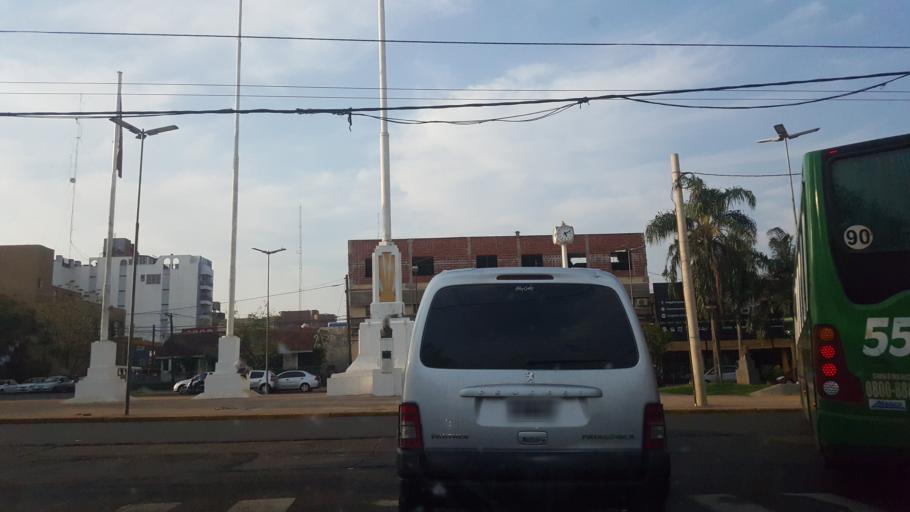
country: AR
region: Misiones
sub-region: Departamento de Capital
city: Posadas
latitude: -27.3745
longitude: -55.8986
